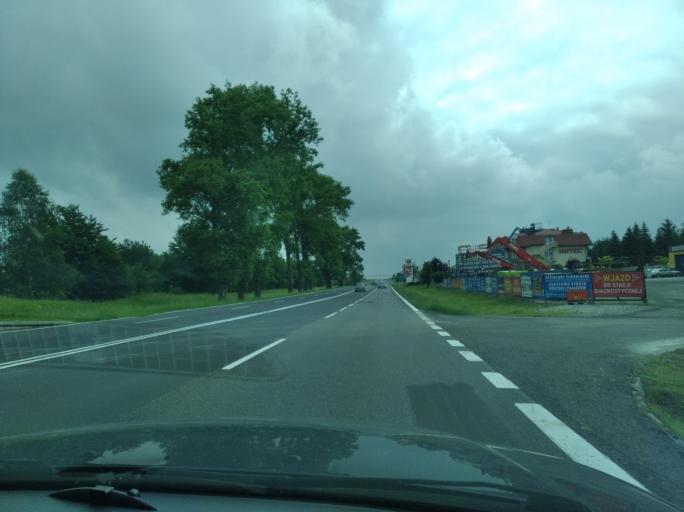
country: PL
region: Subcarpathian Voivodeship
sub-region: Powiat przeworski
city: Rozborz
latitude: 50.0511
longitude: 22.5244
